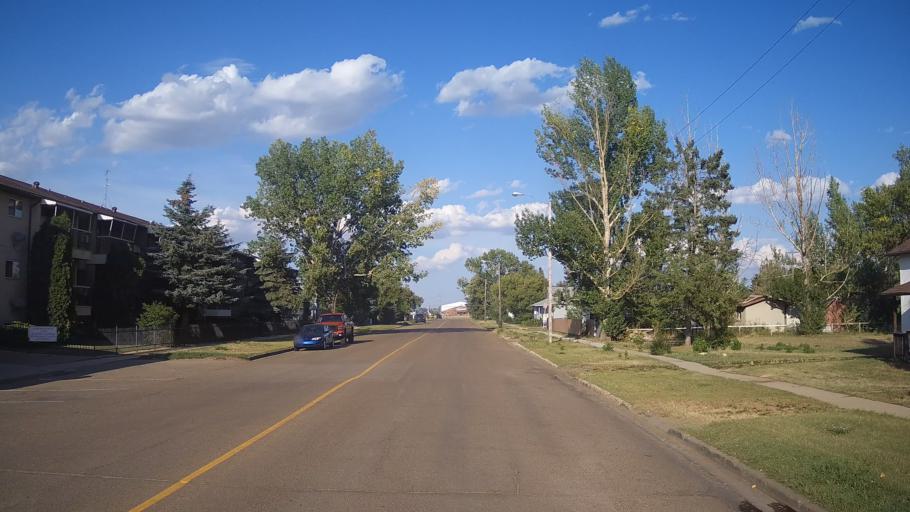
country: CA
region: Alberta
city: Hanna
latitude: 51.6437
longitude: -111.9245
